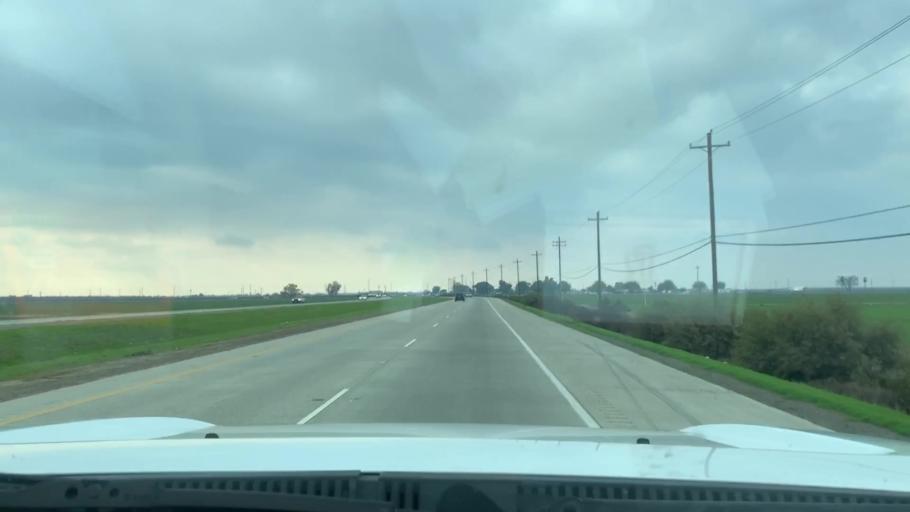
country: US
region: California
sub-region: Kings County
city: Home Garden
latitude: 36.3285
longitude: -119.5722
